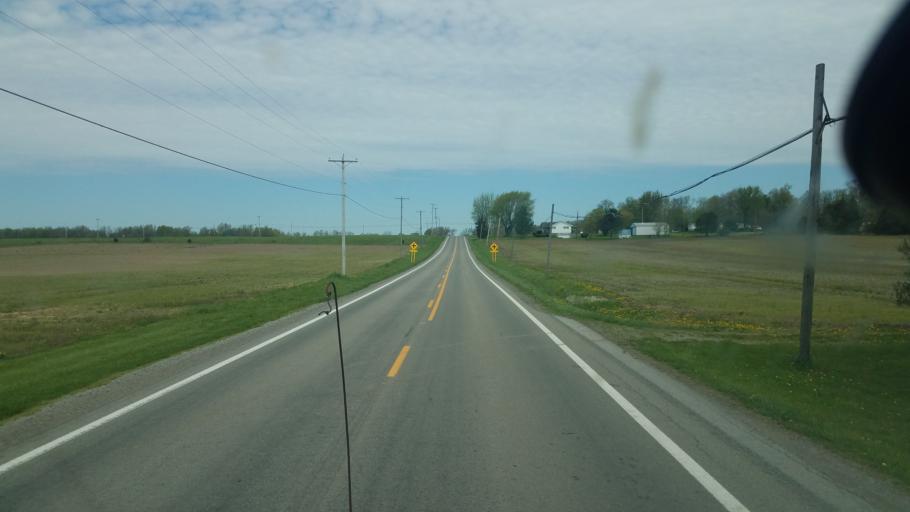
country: US
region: Ohio
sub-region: Hardin County
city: Ada
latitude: 40.7044
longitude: -83.7852
